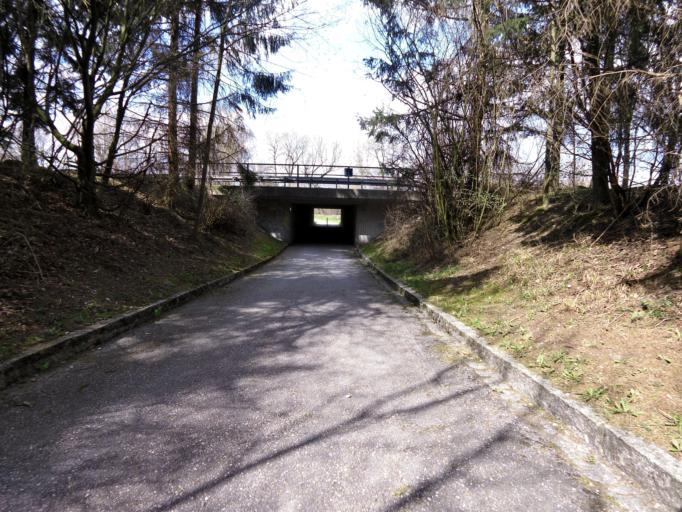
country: DE
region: Bavaria
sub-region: Lower Bavaria
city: Eching
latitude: 48.5111
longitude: 12.0472
